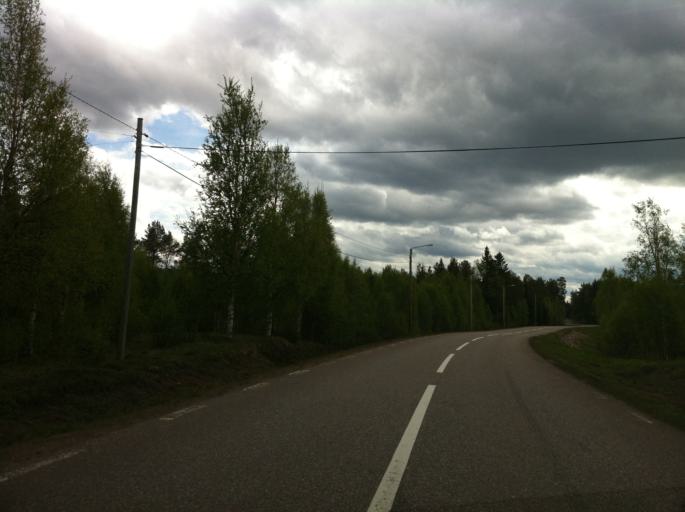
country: NO
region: Hedmark
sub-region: Trysil
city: Innbygda
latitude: 61.4195
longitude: 13.0861
